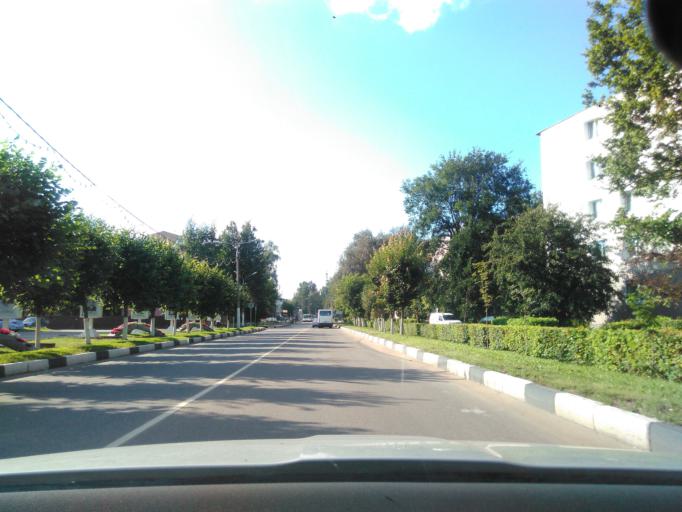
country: RU
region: Moskovskaya
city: Klin
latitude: 56.3222
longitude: 36.7214
